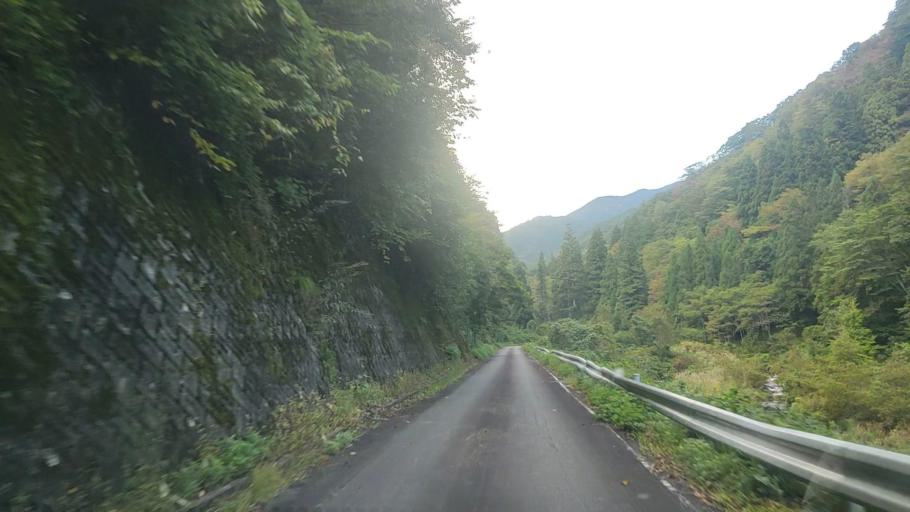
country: JP
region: Gifu
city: Takayama
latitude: 36.3147
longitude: 137.0845
